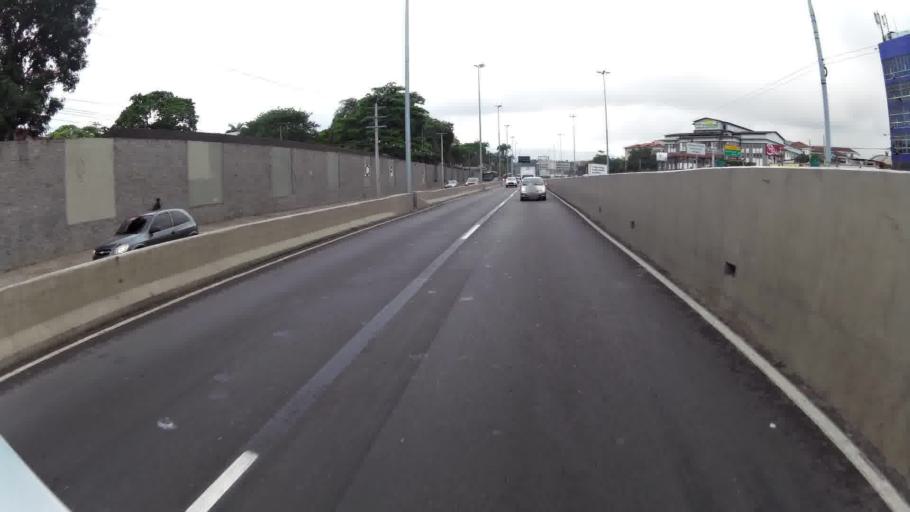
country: BR
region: Rio de Janeiro
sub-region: Rio De Janeiro
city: Rio de Janeiro
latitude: -22.8650
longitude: -43.2477
